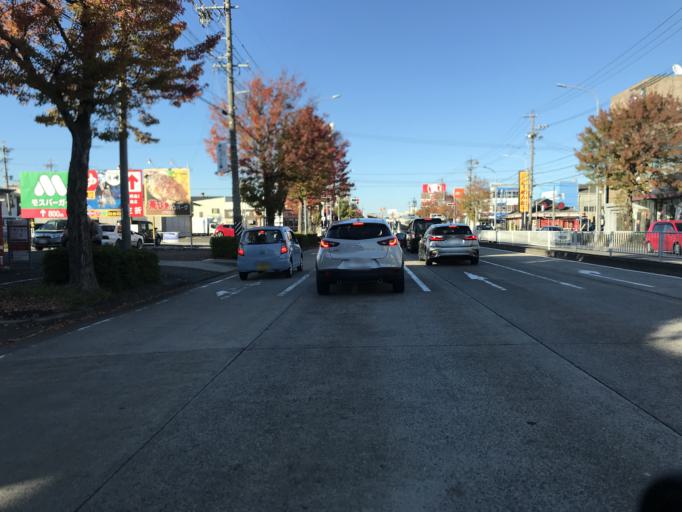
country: JP
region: Aichi
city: Nagoya-shi
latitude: 35.1308
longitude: 136.8689
